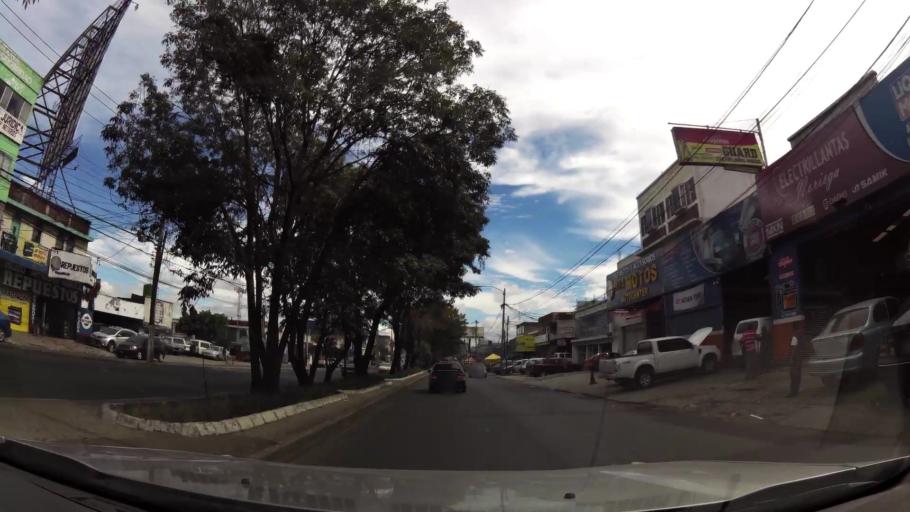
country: GT
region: Guatemala
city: Mixco
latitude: 14.6438
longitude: -90.5739
